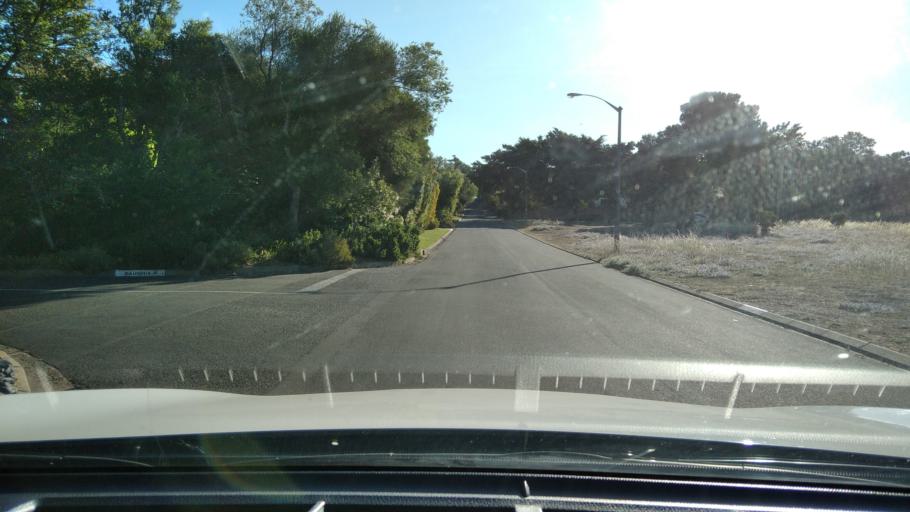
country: ZA
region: Western Cape
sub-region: City of Cape Town
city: Kraaifontein
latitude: -33.8192
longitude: 18.6624
